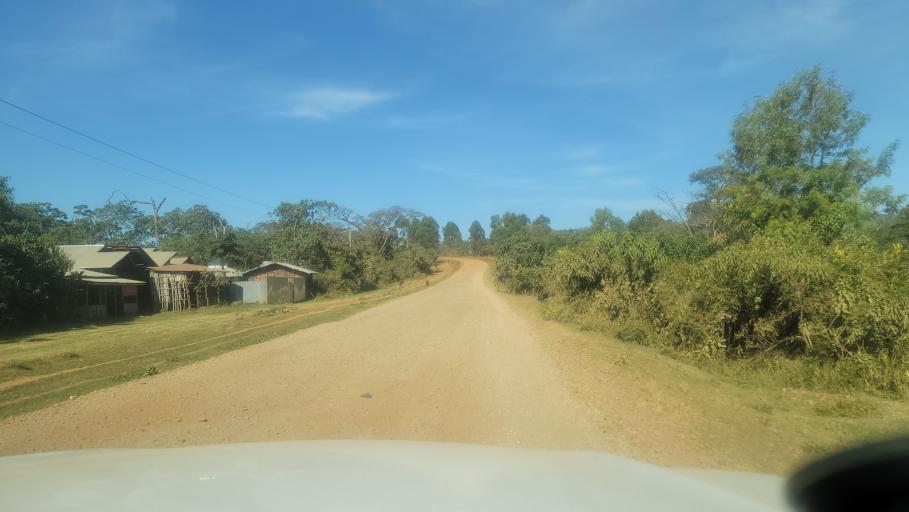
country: ET
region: Oromiya
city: Agaro
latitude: 7.7964
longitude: 36.4917
